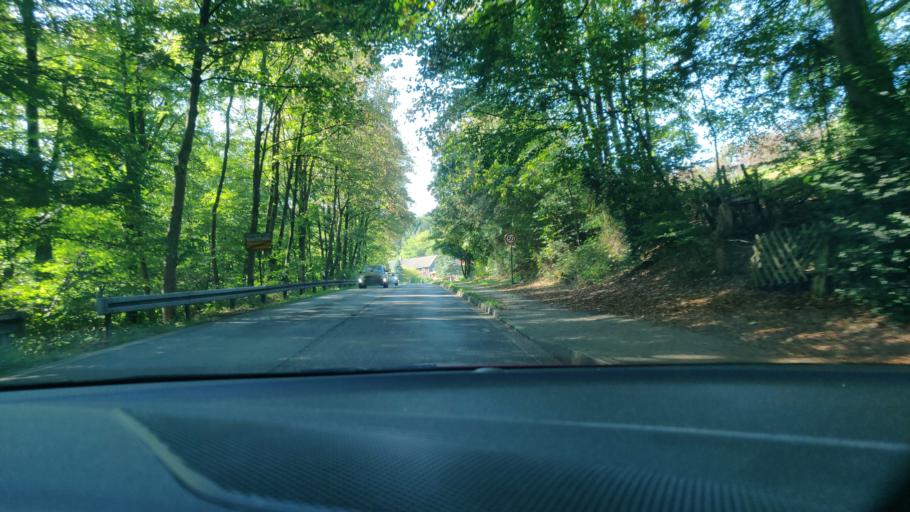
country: DE
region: North Rhine-Westphalia
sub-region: Regierungsbezirk Dusseldorf
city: Velbert
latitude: 51.3482
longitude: 7.0997
